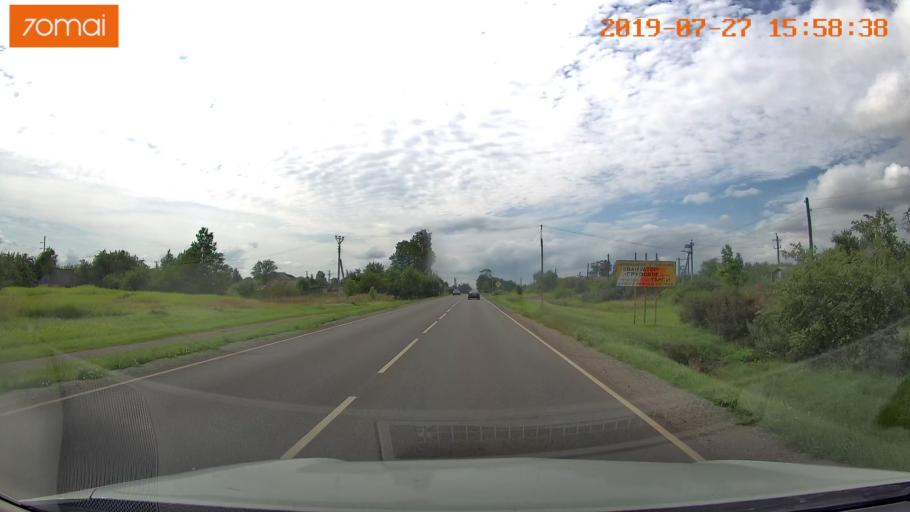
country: RU
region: Kaliningrad
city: Chernyakhovsk
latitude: 54.6264
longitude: 21.8605
